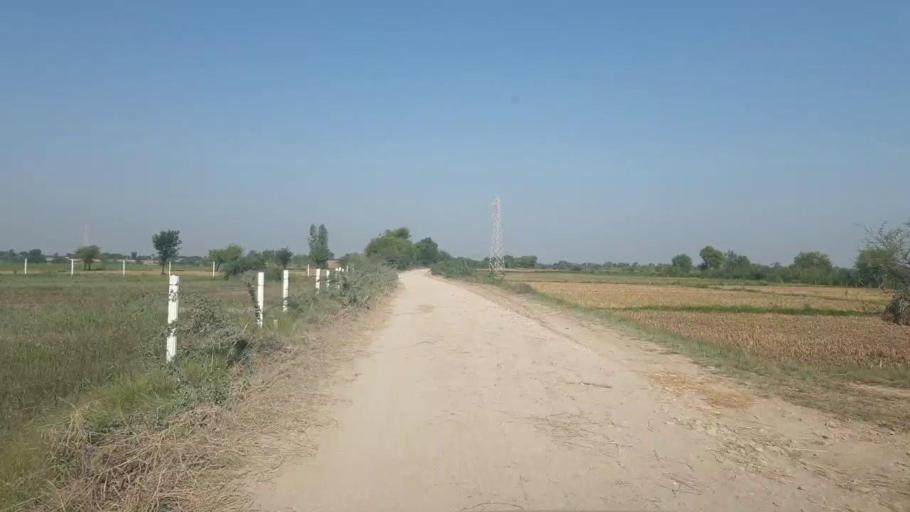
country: PK
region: Sindh
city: Badin
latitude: 24.6718
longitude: 68.8589
